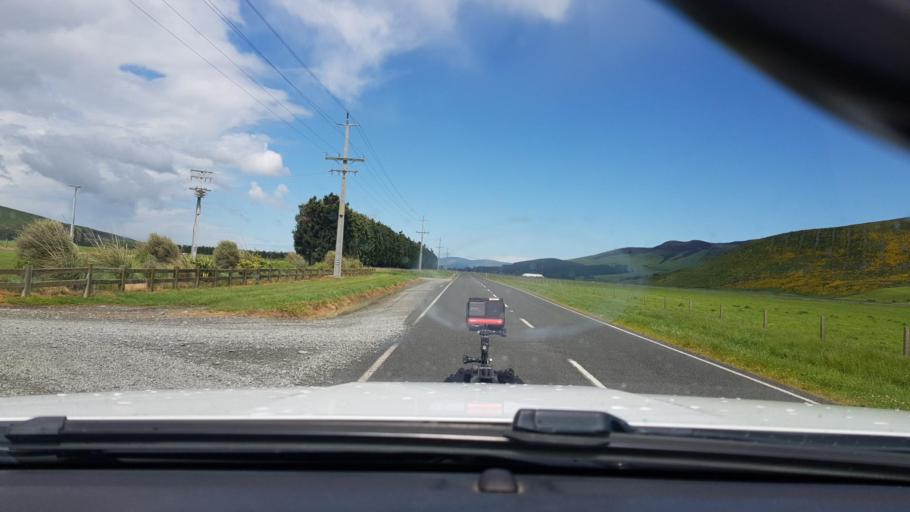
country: NZ
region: Southland
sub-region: Southland District
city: Winton
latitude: -45.7816
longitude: 168.3955
